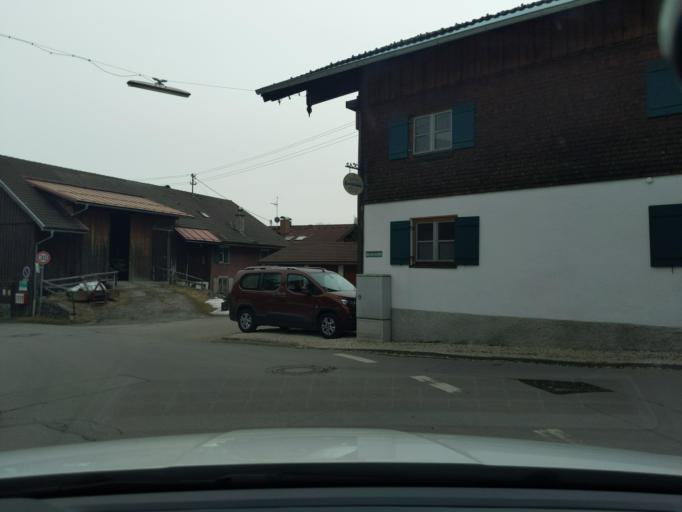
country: DE
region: Bavaria
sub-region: Swabia
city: Bolsterlang
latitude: 47.4610
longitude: 10.2321
